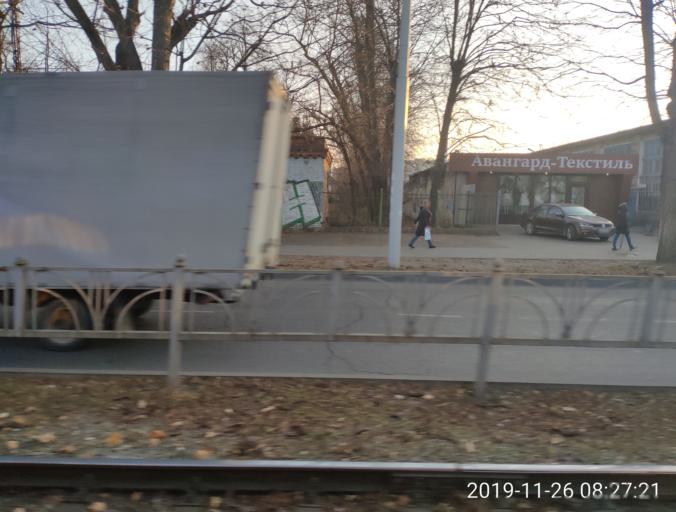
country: RU
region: Krasnodarskiy
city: Krasnodar
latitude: 45.0575
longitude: 39.0023
